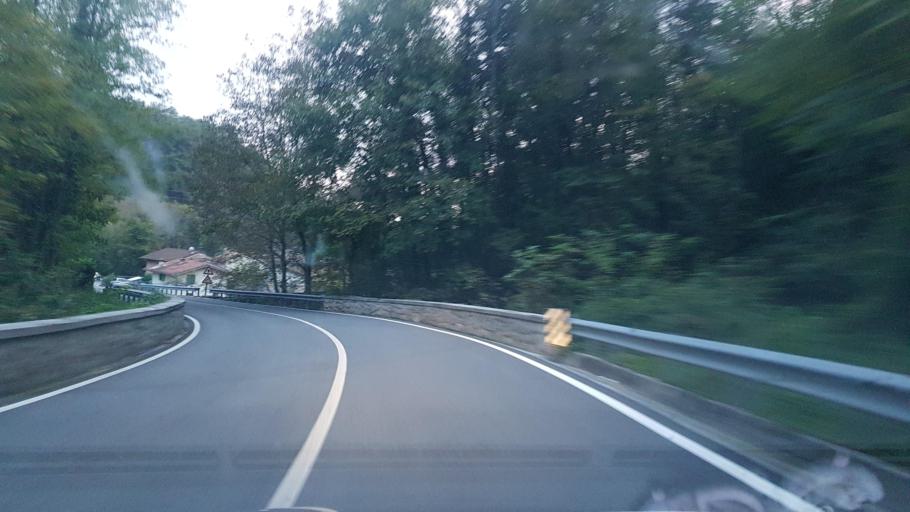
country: IT
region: Friuli Venezia Giulia
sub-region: Provincia di Pordenone
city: Anduins
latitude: 46.2280
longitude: 12.9578
